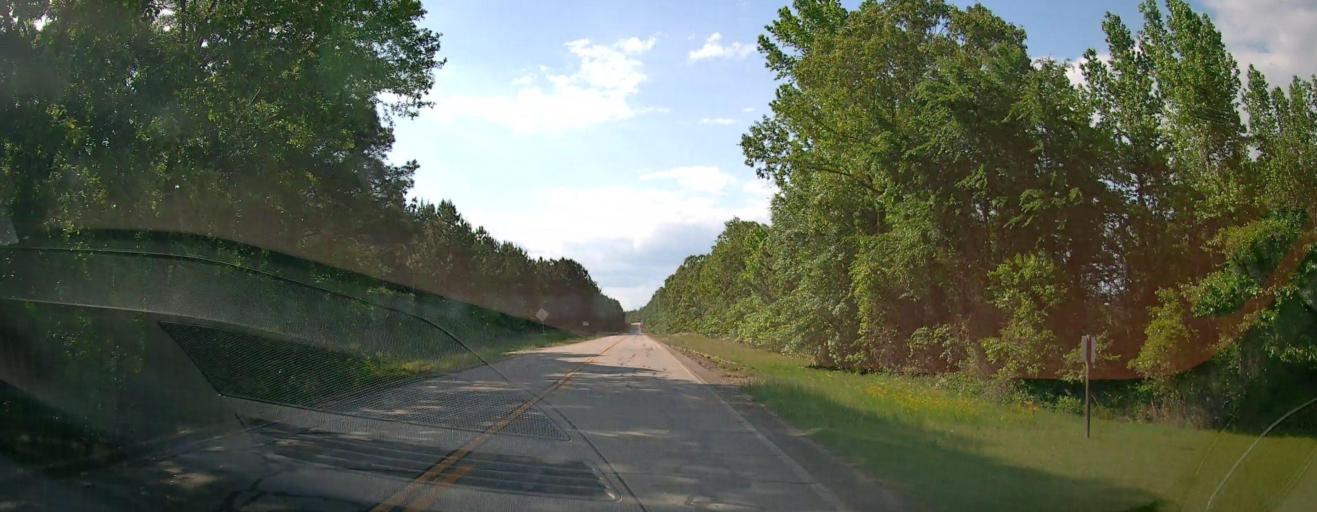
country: US
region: Georgia
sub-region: Washington County
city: Tennille
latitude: 32.9205
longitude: -83.0001
